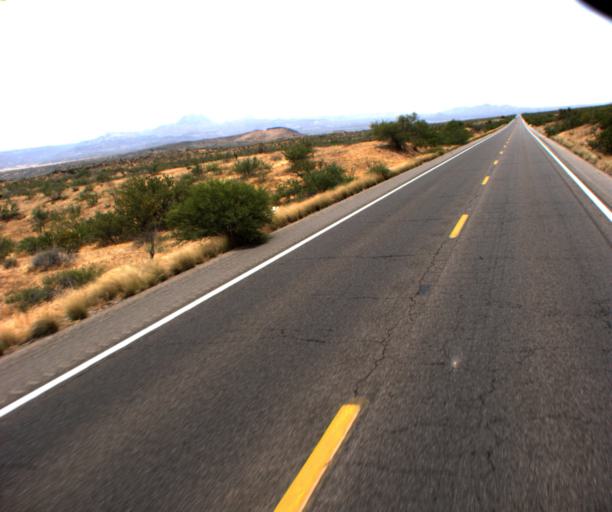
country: US
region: Arizona
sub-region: Gila County
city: Peridot
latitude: 33.3199
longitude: -110.5350
